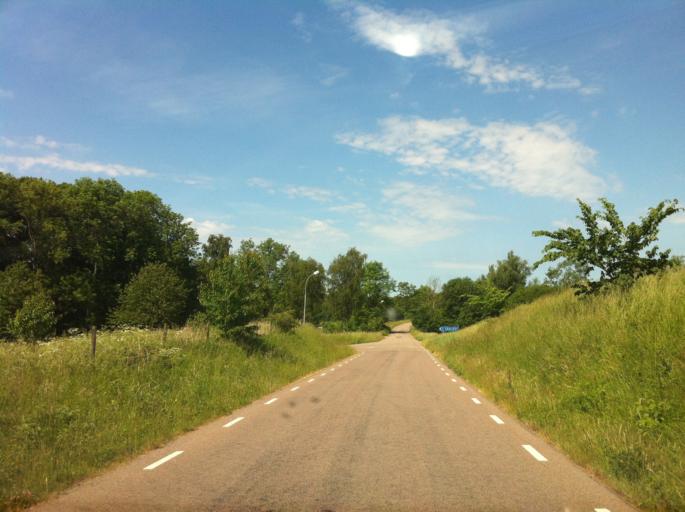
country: SE
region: Skane
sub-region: Landskrona
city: Asmundtorp
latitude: 55.9442
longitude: 12.9206
